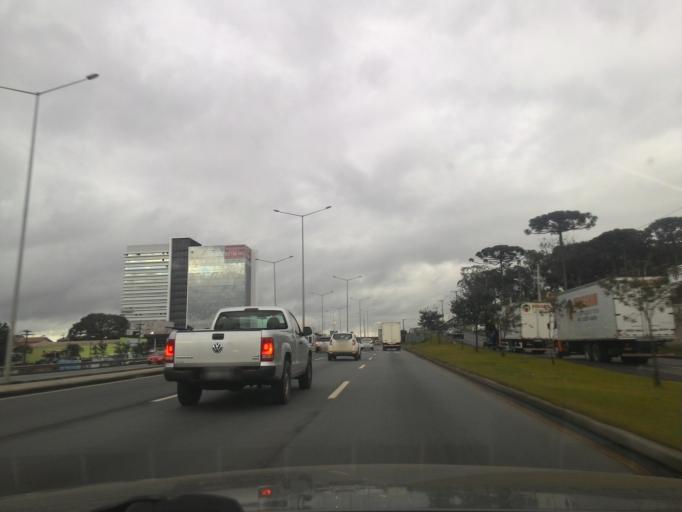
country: BR
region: Parana
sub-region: Curitiba
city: Curitiba
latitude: -25.5006
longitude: -49.2792
